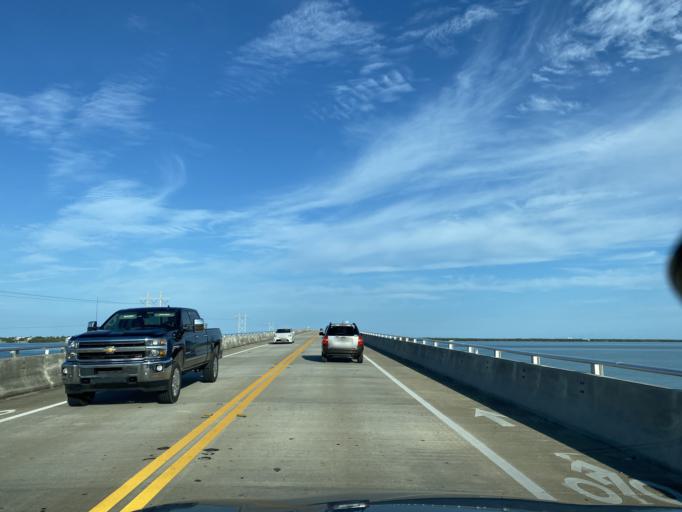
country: US
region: Florida
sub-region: Monroe County
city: Big Pine Key
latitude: 24.6602
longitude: -81.4247
